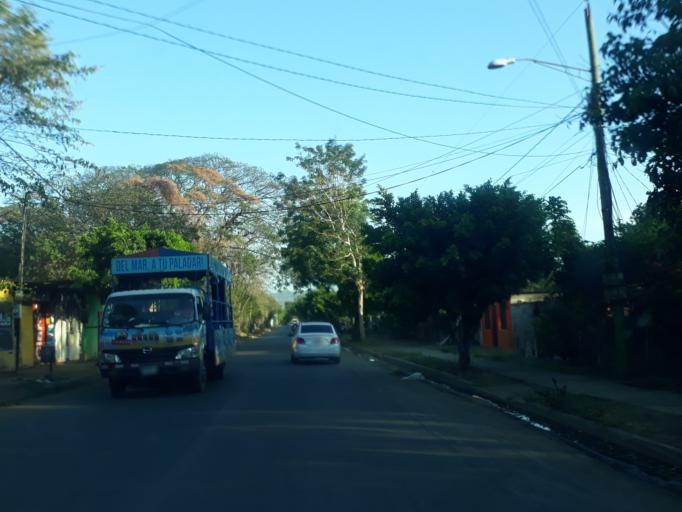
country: NI
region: Masaya
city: Masaya
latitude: 11.9893
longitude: -86.1060
